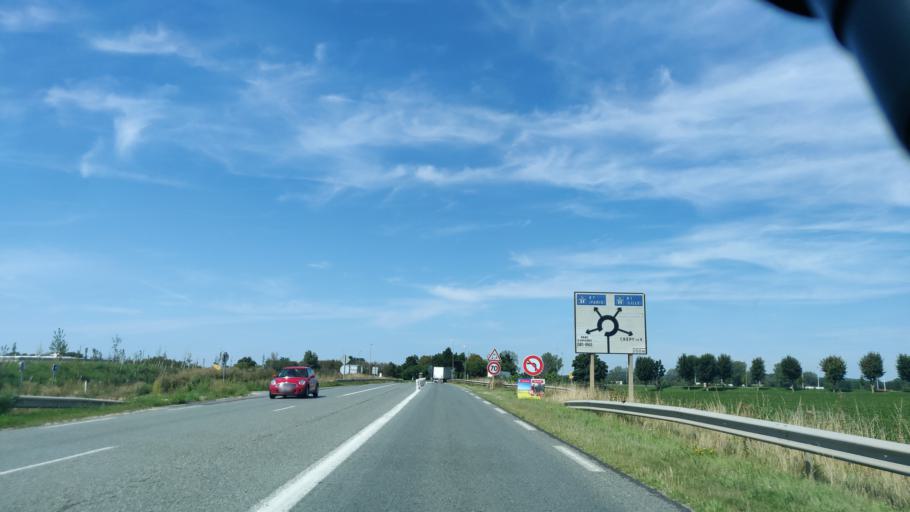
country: FR
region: Picardie
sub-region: Departement de l'Oise
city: Chamant
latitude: 49.2089
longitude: 2.6262
